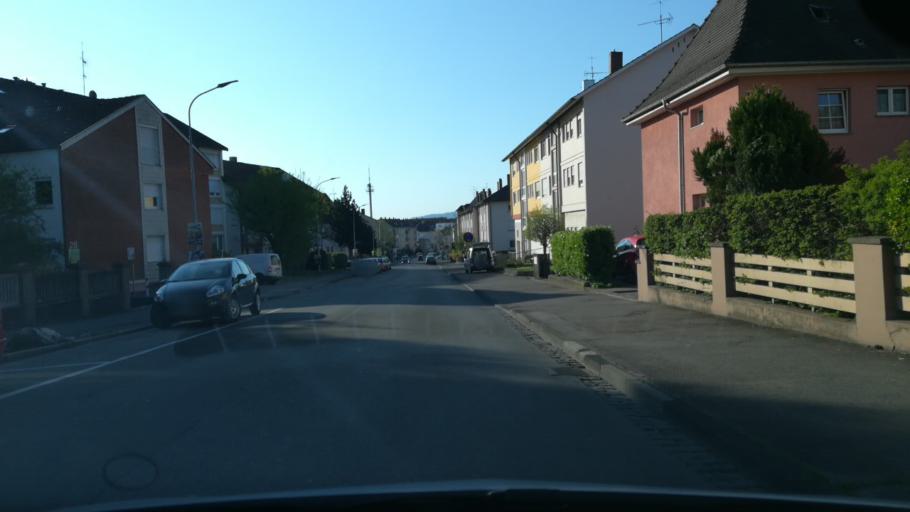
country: DE
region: Baden-Wuerttemberg
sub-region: Freiburg Region
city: Singen
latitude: 47.7665
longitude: 8.8416
